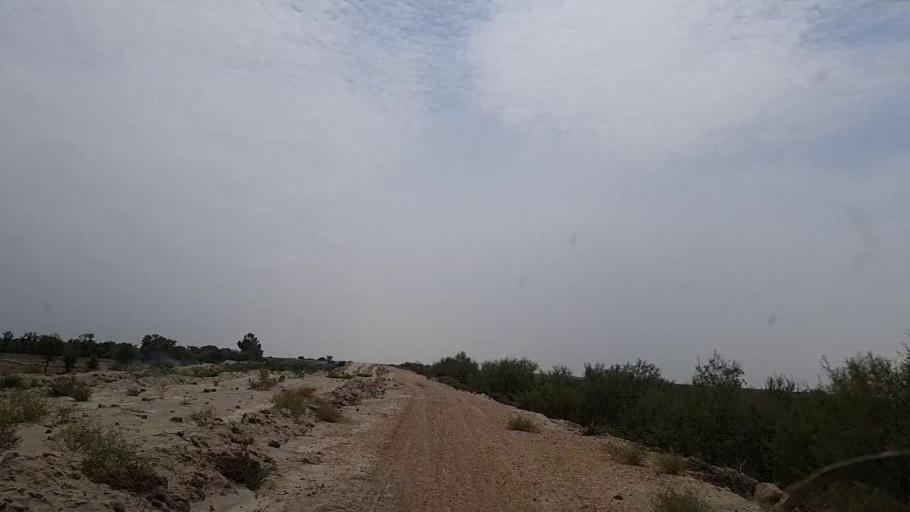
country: PK
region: Sindh
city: Phulji
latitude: 26.8496
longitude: 67.6214
